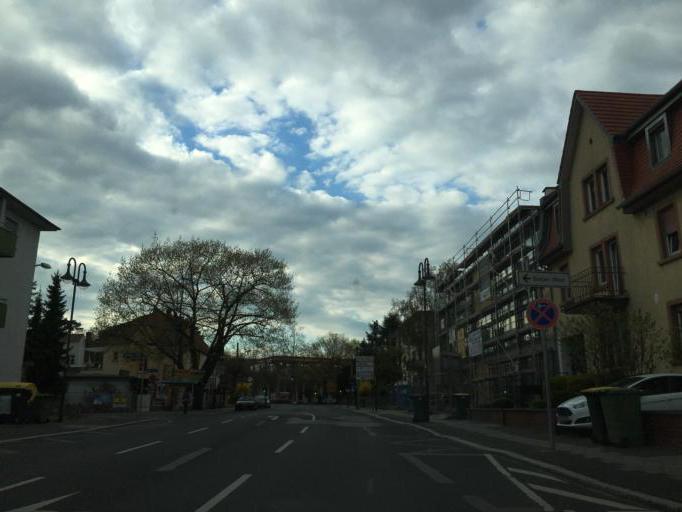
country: DE
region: Hesse
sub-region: Regierungsbezirk Darmstadt
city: Offenbach
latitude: 50.0919
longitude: 8.8012
